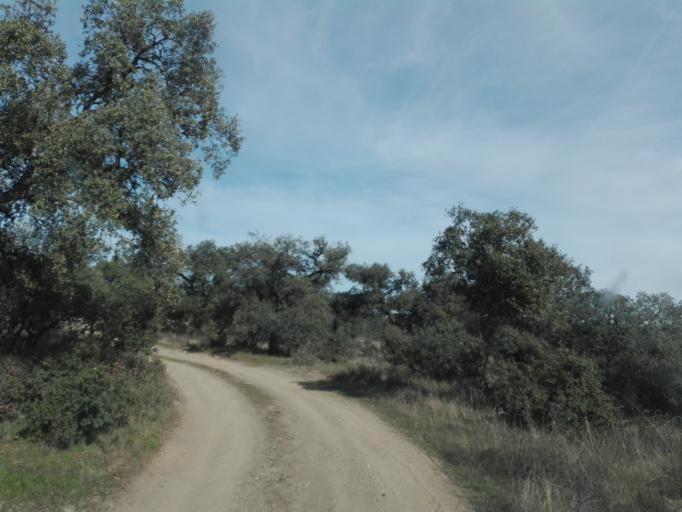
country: ES
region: Extremadura
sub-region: Provincia de Badajoz
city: Azuaga
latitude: 38.2246
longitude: -5.7395
